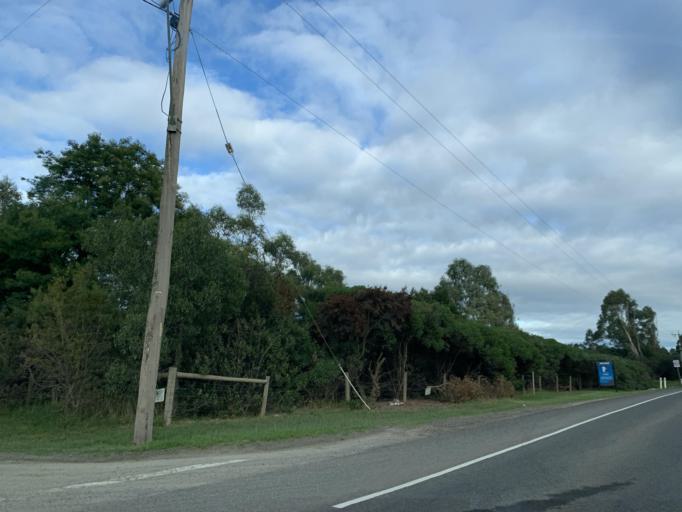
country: AU
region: Victoria
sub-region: Cardinia
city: Officer South
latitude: -38.1430
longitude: 145.3993
